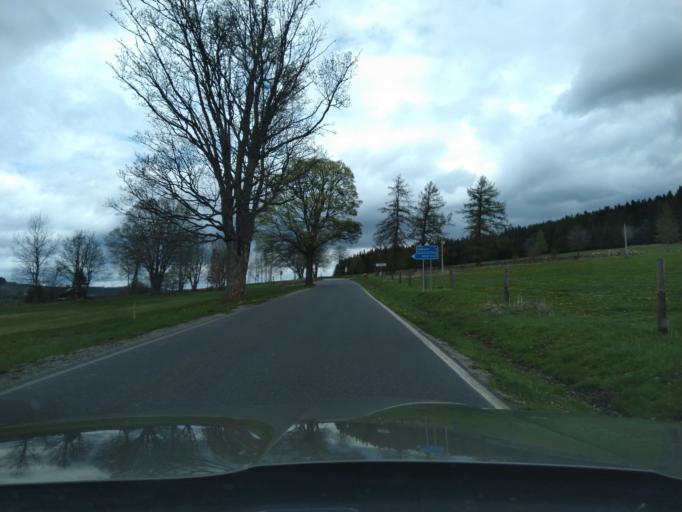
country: CZ
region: Jihocesky
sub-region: Okres Prachatice
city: Borova Lada
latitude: 49.0275
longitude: 13.6665
